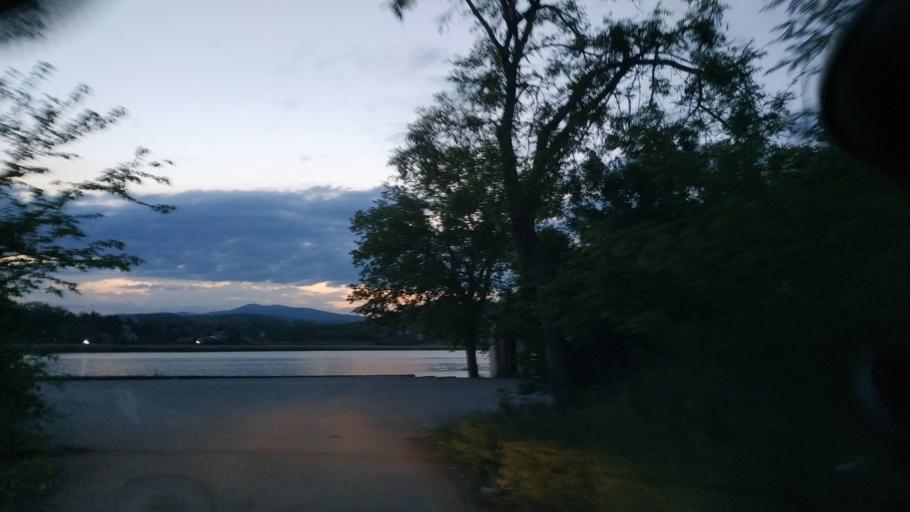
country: RS
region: Central Serbia
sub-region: Nisavski Okrug
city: Merosina
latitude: 43.3028
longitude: 21.6810
